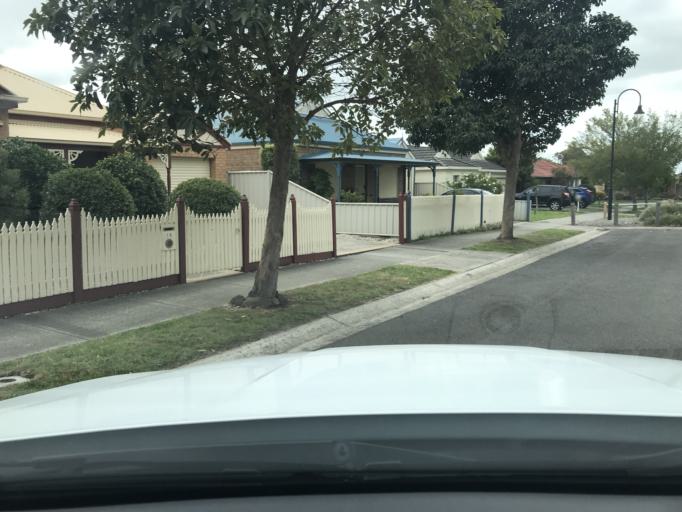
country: AU
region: Victoria
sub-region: Hume
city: Craigieburn
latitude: -37.5891
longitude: 144.9340
